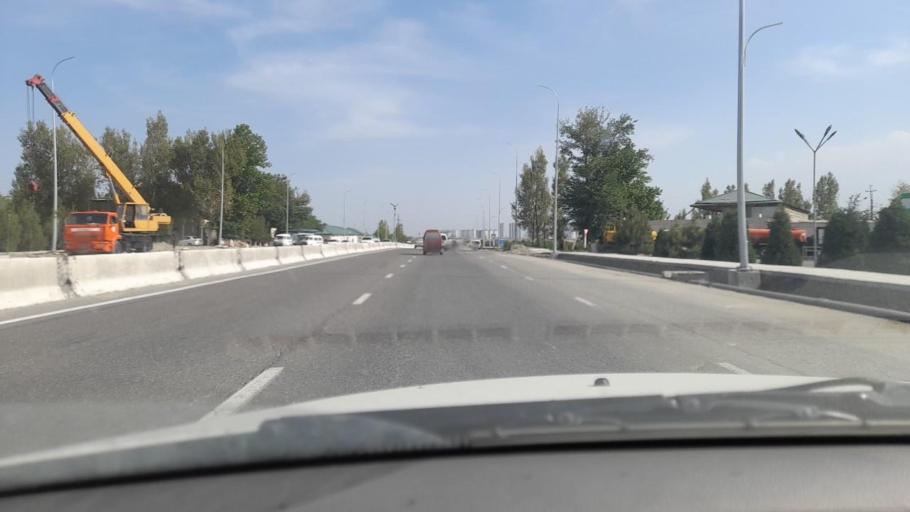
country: UZ
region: Samarqand
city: Daxbet
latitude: 39.7458
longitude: 66.9237
